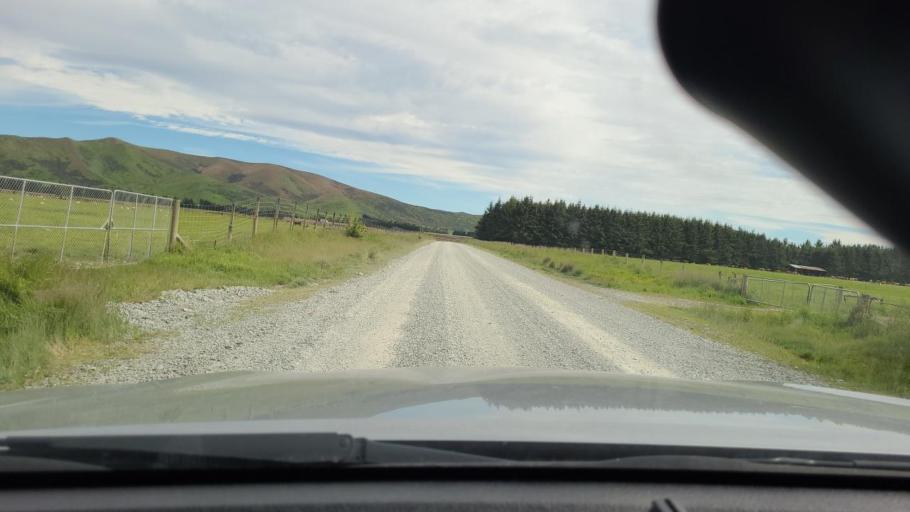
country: NZ
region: Southland
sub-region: Southland District
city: Te Anau
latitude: -45.5325
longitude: 167.9620
